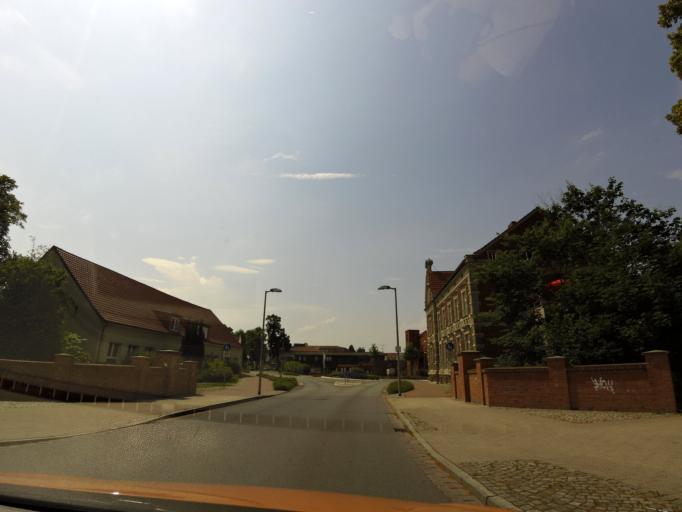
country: DE
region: Brandenburg
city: Pritzwalk
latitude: 53.1494
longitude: 12.1731
